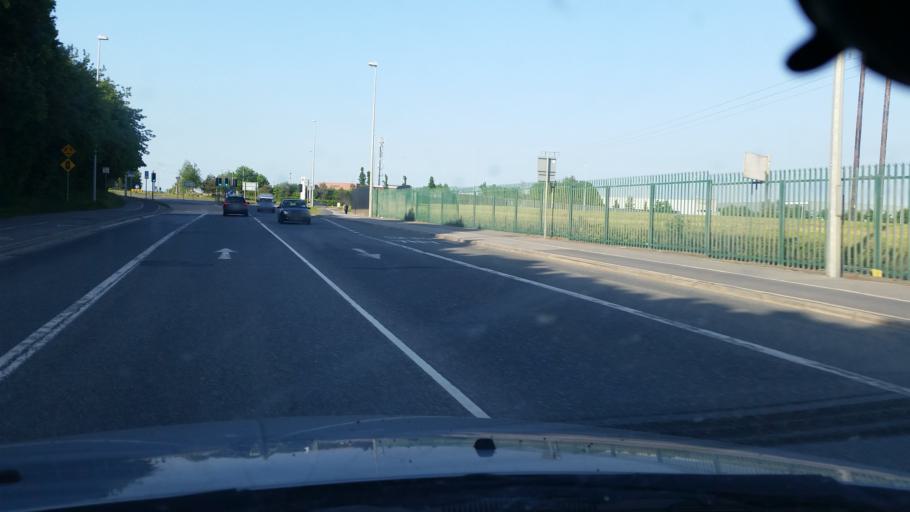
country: IE
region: Leinster
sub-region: Fingal County
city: Blanchardstown
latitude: 53.4027
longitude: -6.3607
